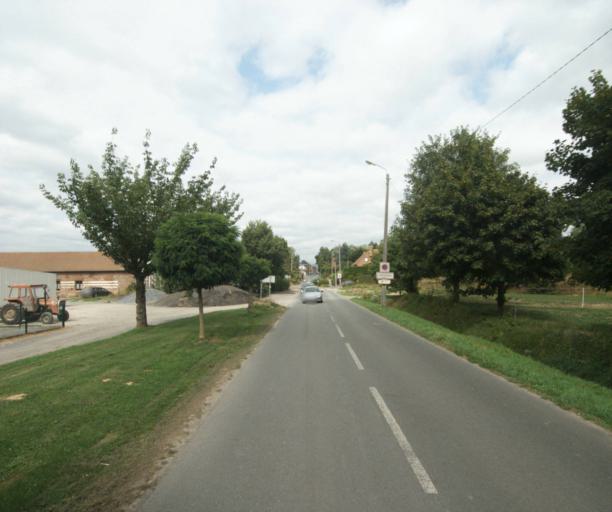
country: FR
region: Nord-Pas-de-Calais
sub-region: Departement du Nord
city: Chereng
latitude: 50.6045
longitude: 3.2070
